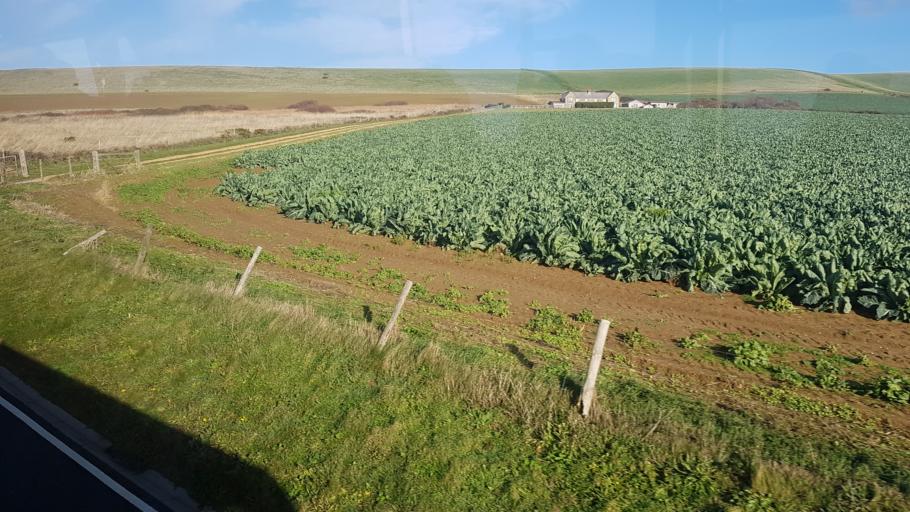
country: GB
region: England
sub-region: Isle of Wight
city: Freshwater
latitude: 50.6565
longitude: -1.4682
